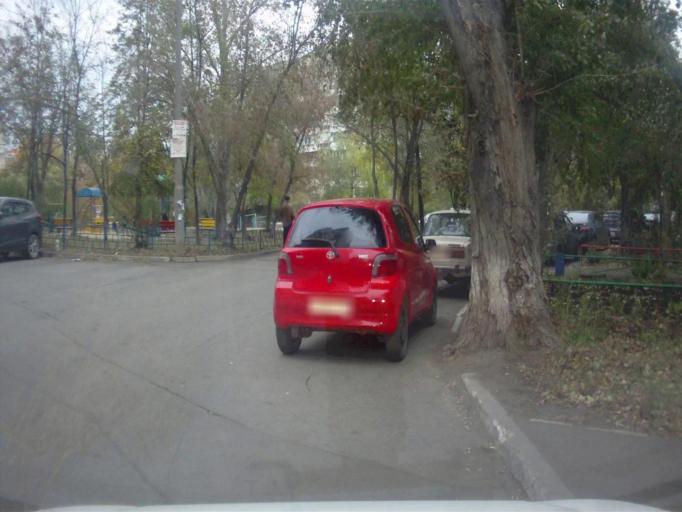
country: RU
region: Chelyabinsk
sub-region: Gorod Chelyabinsk
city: Chelyabinsk
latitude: 55.1803
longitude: 61.3219
